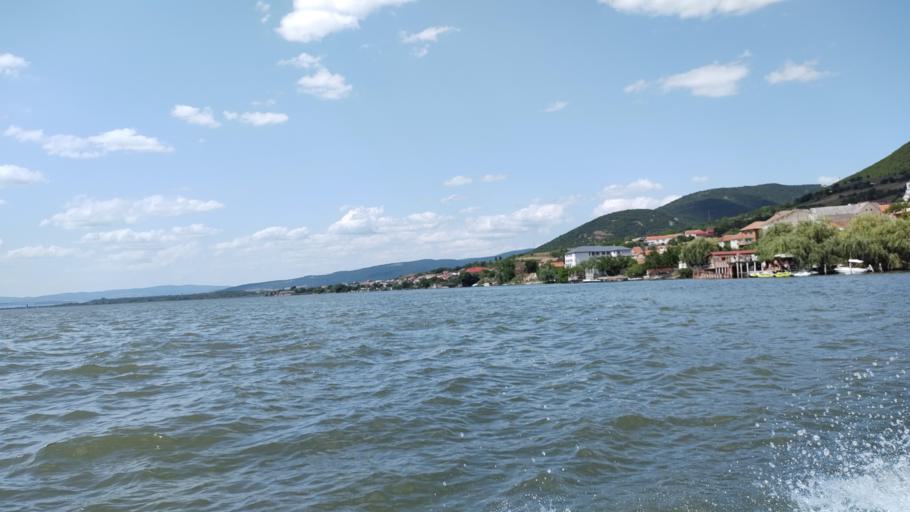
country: RO
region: Caras-Severin
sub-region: Comuna Pescari
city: Coronini
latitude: 44.6758
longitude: 21.6787
